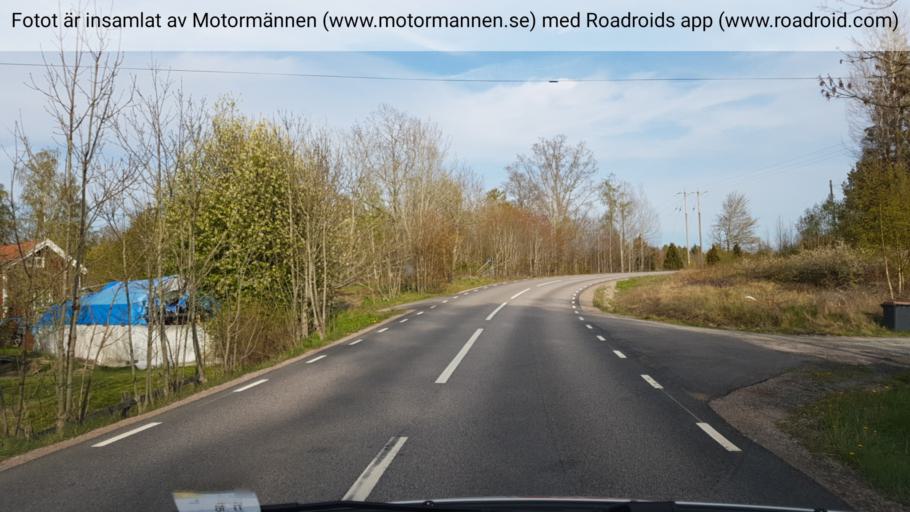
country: SE
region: Kalmar
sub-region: Vasterviks Kommun
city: Vaestervik
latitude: 57.9082
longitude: 16.6609
